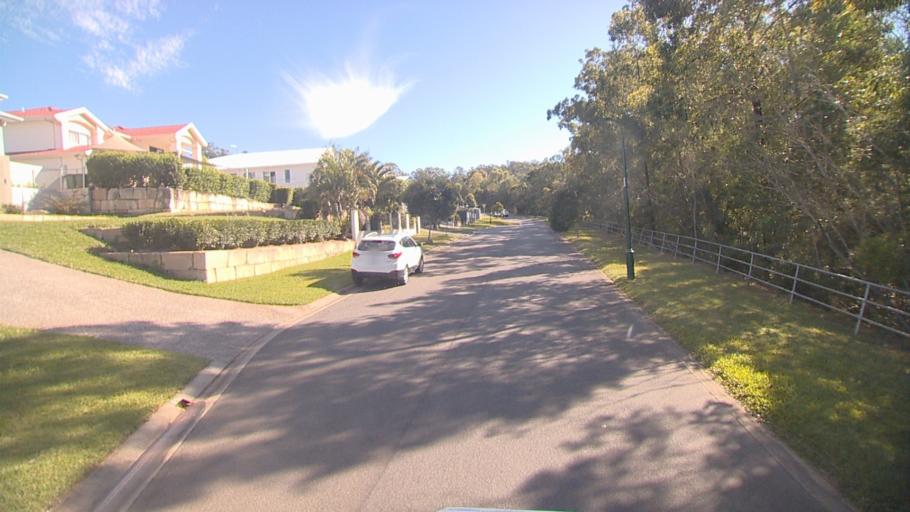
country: AU
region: Queensland
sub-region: Logan
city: Slacks Creek
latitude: -27.6309
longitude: 153.1597
